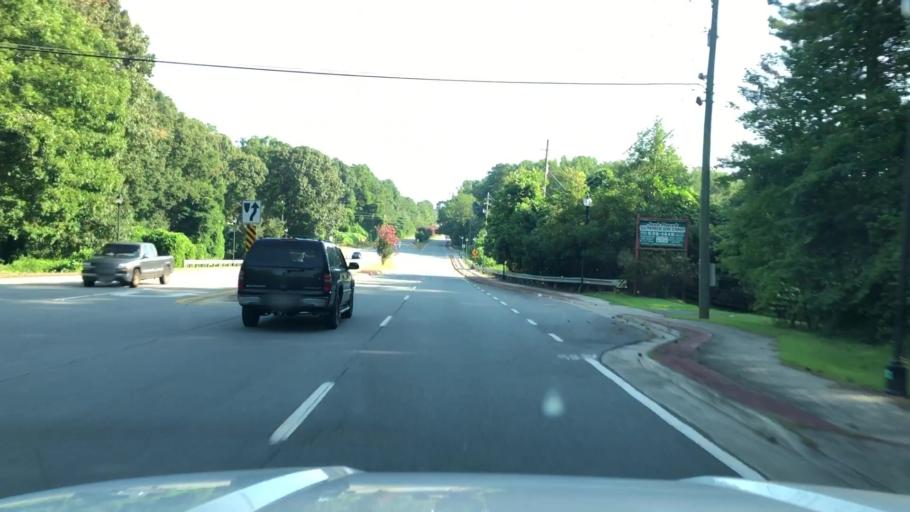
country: US
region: Georgia
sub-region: Cobb County
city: Kennesaw
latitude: 34.0786
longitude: -84.5884
